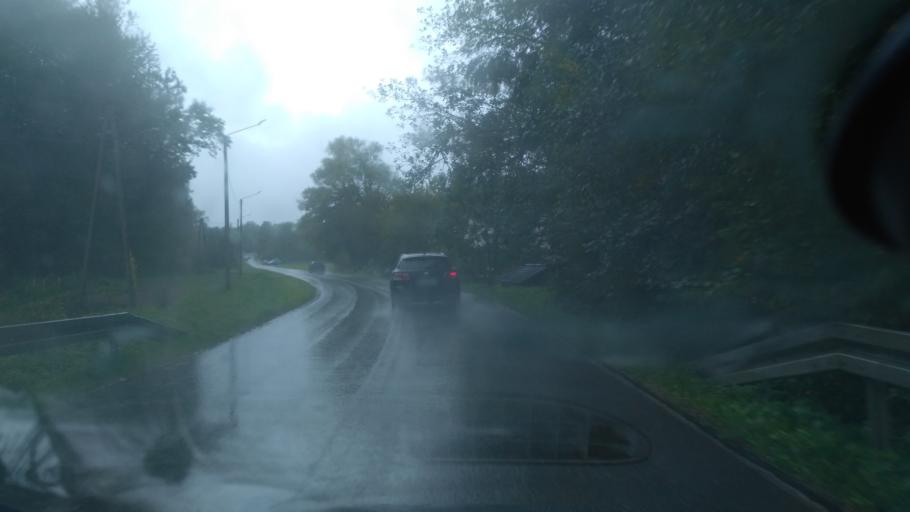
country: PL
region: Subcarpathian Voivodeship
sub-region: Powiat strzyzowski
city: Wisniowa
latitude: 49.9275
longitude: 21.7143
